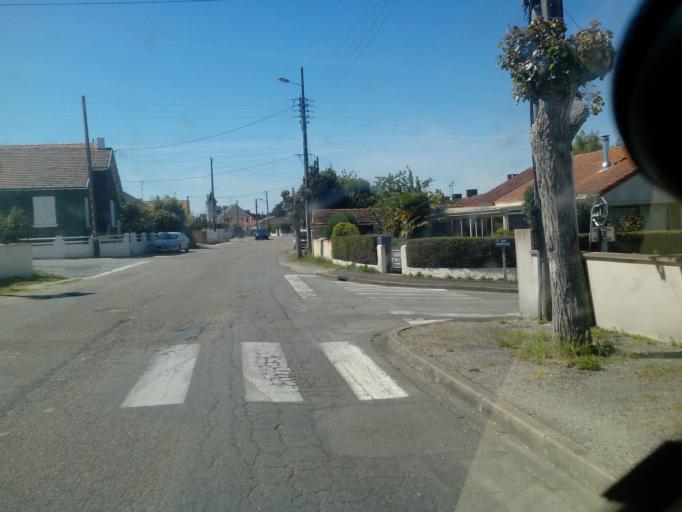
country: FR
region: Pays de la Loire
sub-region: Departement de la Loire-Atlantique
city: Pornic
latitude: 47.1120
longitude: -2.0951
